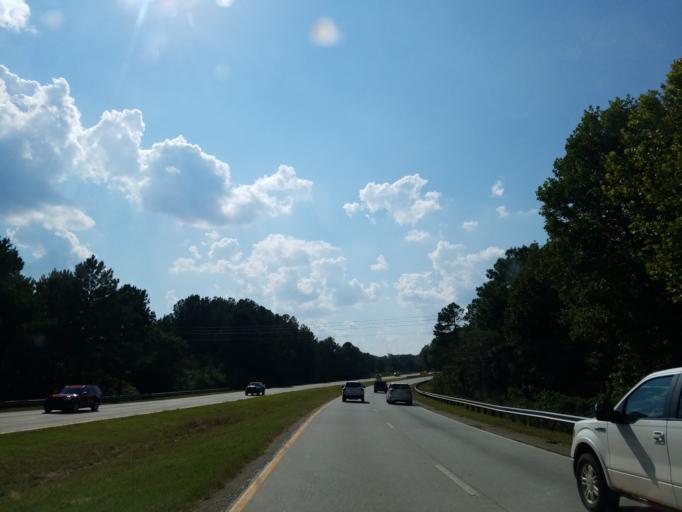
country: US
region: Georgia
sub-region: Clarke County
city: Athens
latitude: 33.9160
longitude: -83.3886
